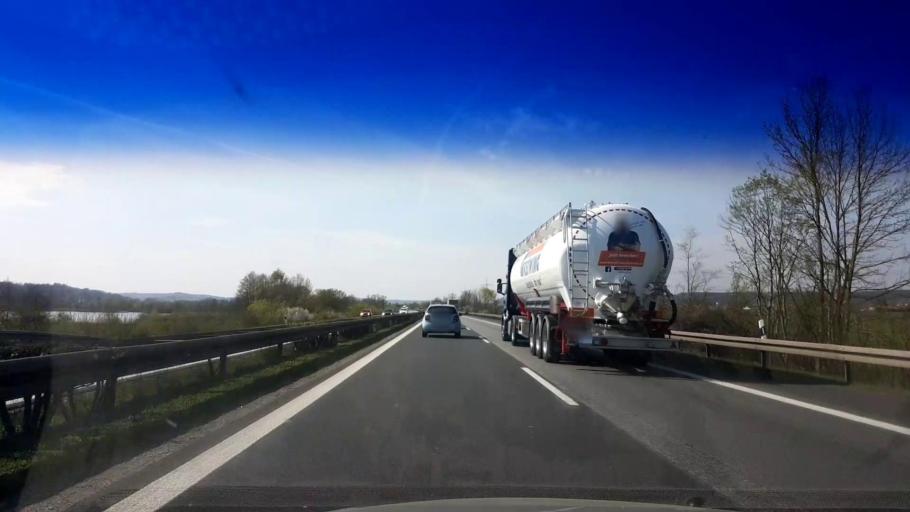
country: DE
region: Bavaria
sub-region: Upper Franconia
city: Bischberg
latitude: 49.9231
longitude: 10.8283
